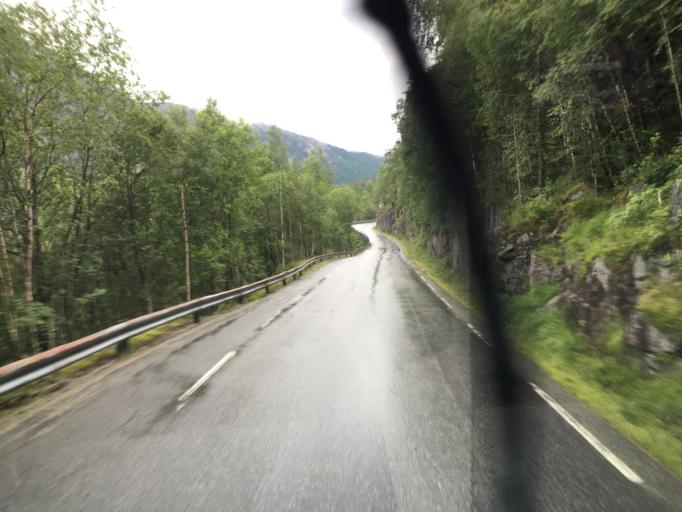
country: NO
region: Rogaland
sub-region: Sauda
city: Sauda
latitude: 59.6743
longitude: 6.4960
